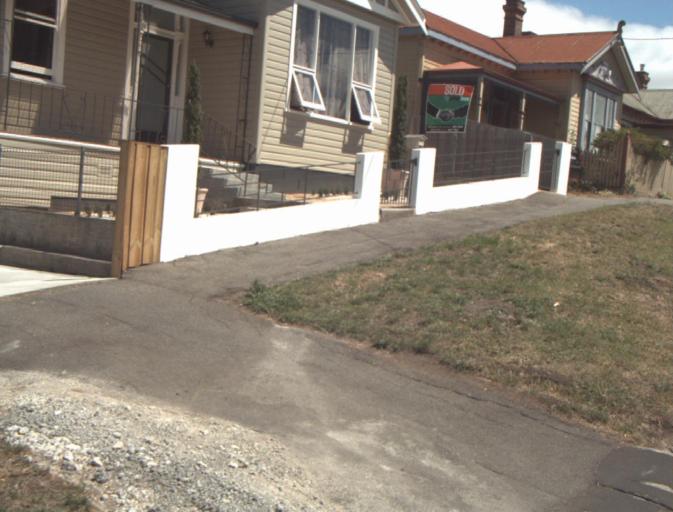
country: AU
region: Tasmania
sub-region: Launceston
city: Launceston
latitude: -41.4228
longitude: 147.1290
